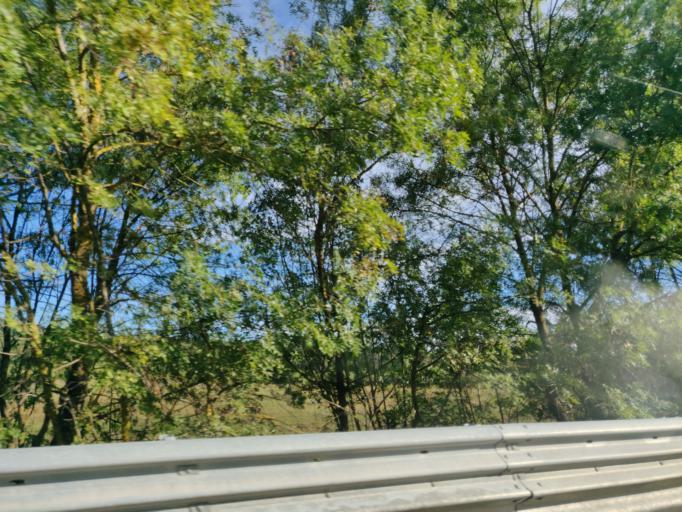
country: IT
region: Tuscany
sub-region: Provincia di Grosseto
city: Ribolla
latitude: 42.9228
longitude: 10.9915
